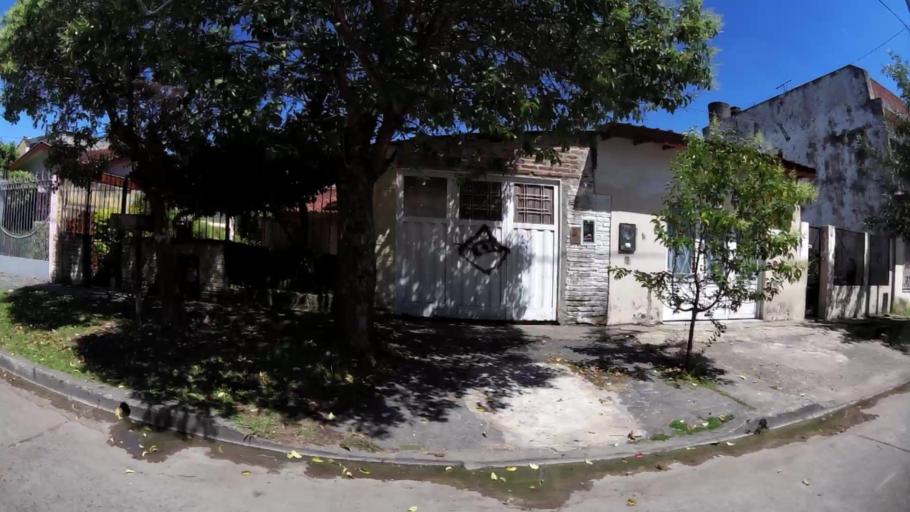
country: AR
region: Buenos Aires
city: Ituzaingo
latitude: -34.6749
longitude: -58.6596
